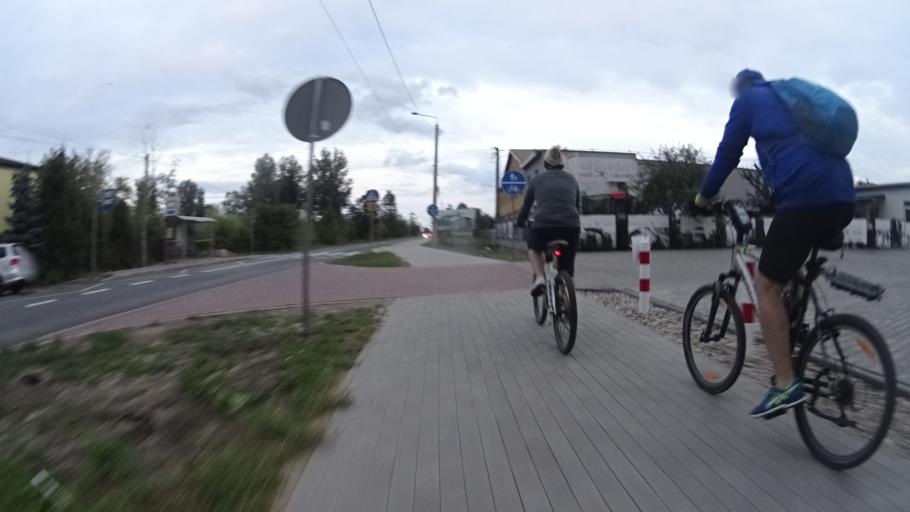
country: PL
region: Masovian Voivodeship
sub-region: Powiat warszawski zachodni
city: Ozarow Mazowiecki
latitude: 52.2304
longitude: 20.7839
